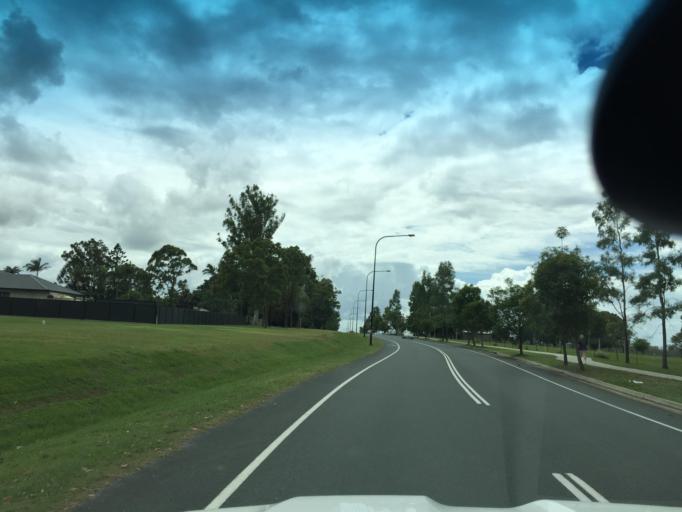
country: AU
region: Queensland
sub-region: Moreton Bay
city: Burpengary
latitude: -27.1277
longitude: 152.9892
